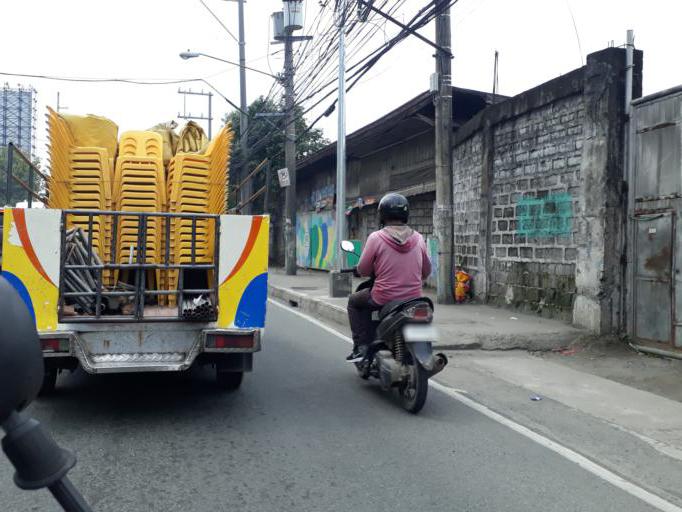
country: PH
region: Calabarzon
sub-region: Province of Rizal
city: Valenzuela
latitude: 14.6836
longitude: 120.9775
